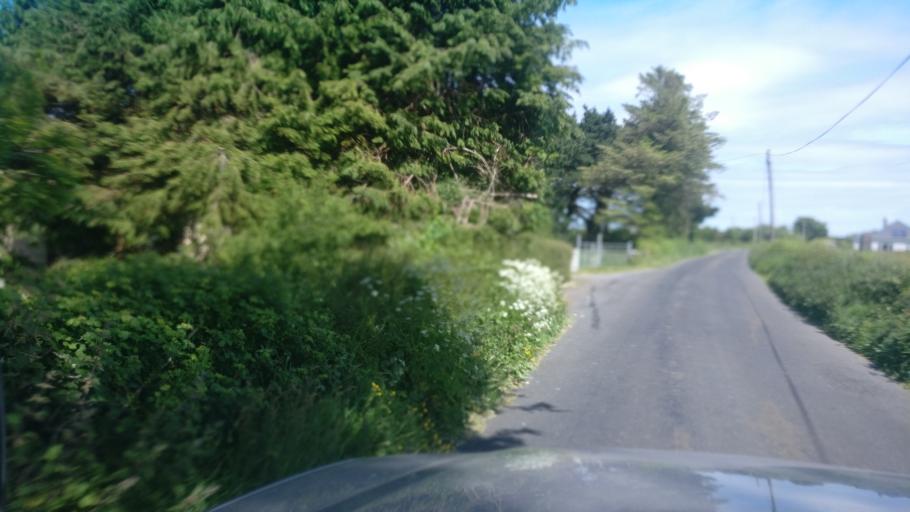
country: IE
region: Connaught
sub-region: County Galway
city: Gort
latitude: 53.1472
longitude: -8.7581
